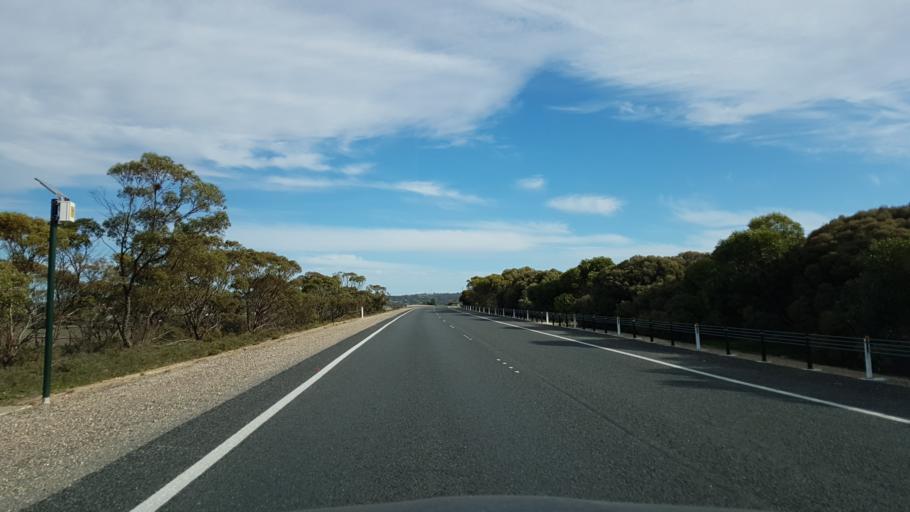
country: AU
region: South Australia
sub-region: Murray Bridge
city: Murray Bridge
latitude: -35.1497
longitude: 139.2672
